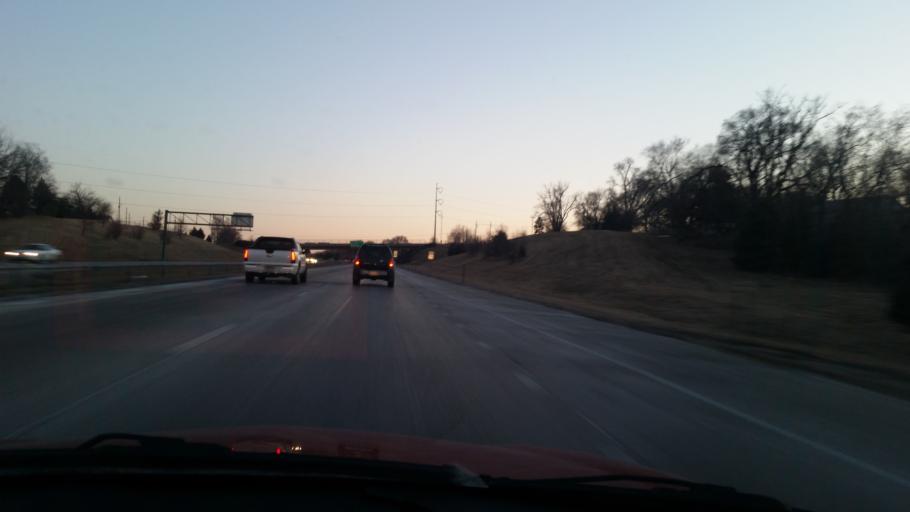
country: US
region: Nebraska
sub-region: Sarpy County
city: Offutt Air Force Base
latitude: 41.1793
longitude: -95.9392
